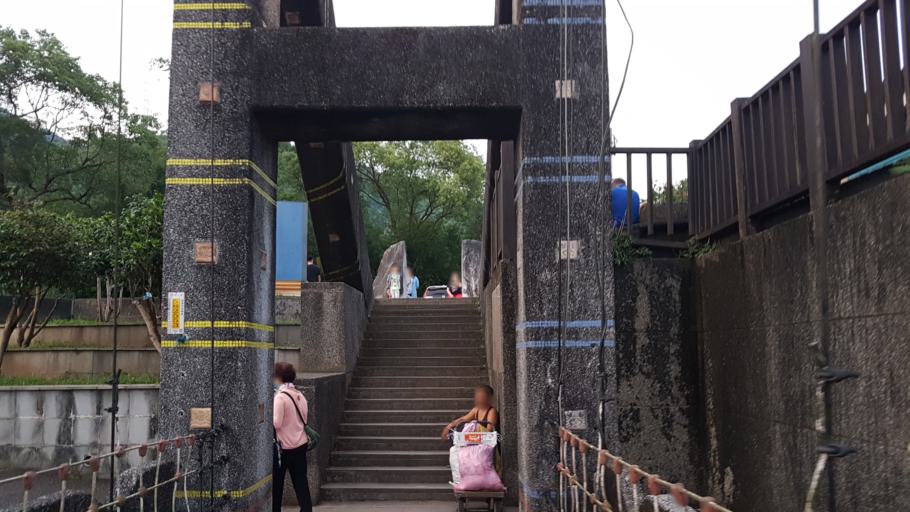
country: TW
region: Taiwan
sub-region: Yilan
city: Yilan
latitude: 24.9354
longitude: 121.7043
